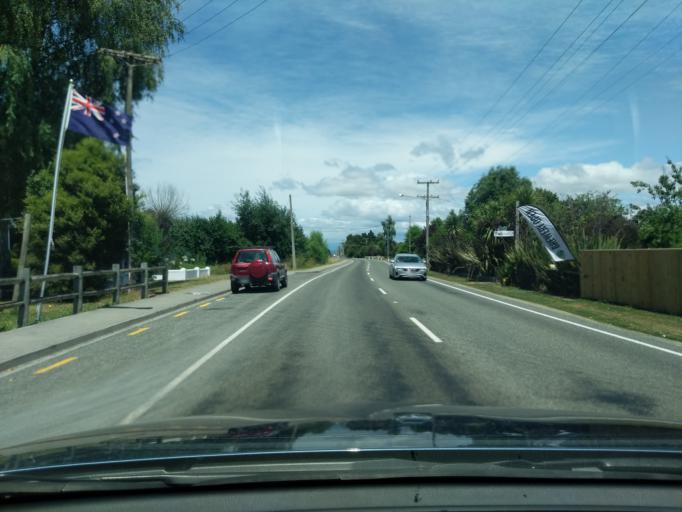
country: NZ
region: Tasman
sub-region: Tasman District
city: Motueka
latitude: -41.0800
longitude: 172.9973
